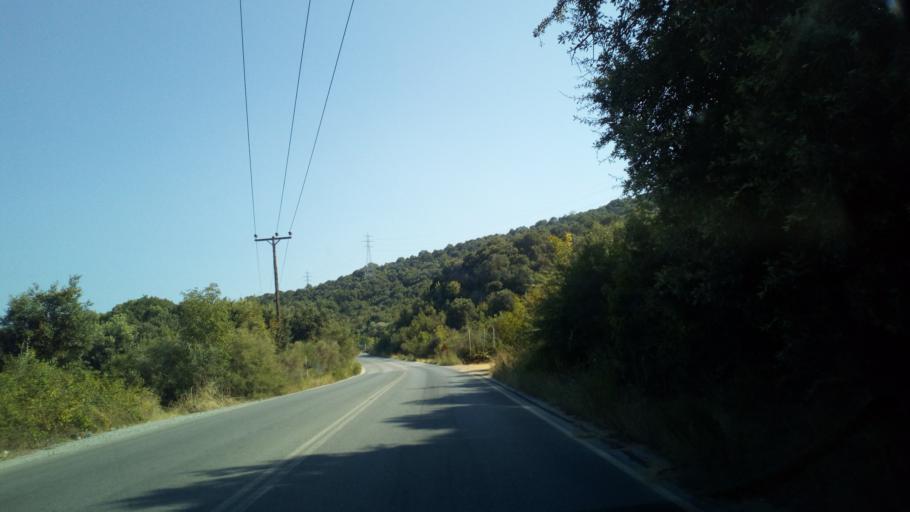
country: GR
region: Central Macedonia
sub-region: Nomos Thessalonikis
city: Stavros
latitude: 40.6363
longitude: 23.7539
